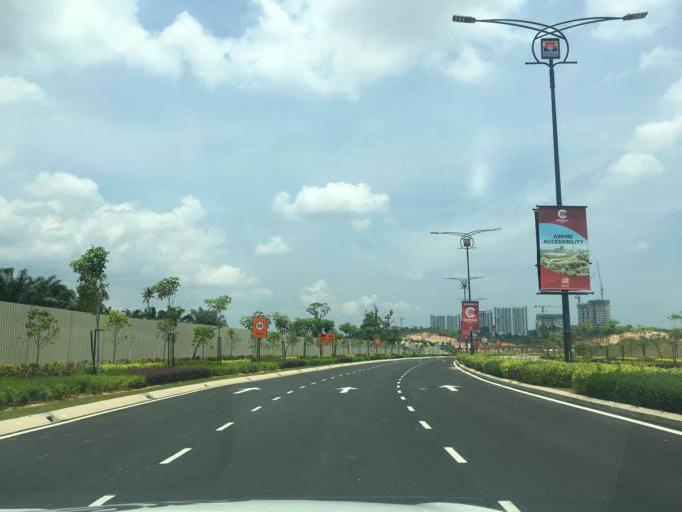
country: MY
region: Putrajaya
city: Putrajaya
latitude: 2.8495
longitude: 101.6970
